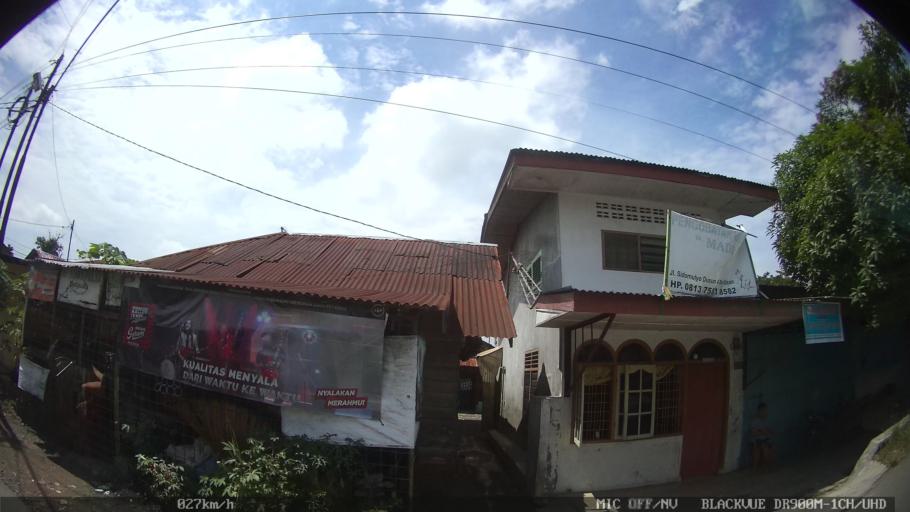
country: ID
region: North Sumatra
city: Percut
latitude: 3.6019
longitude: 98.7783
